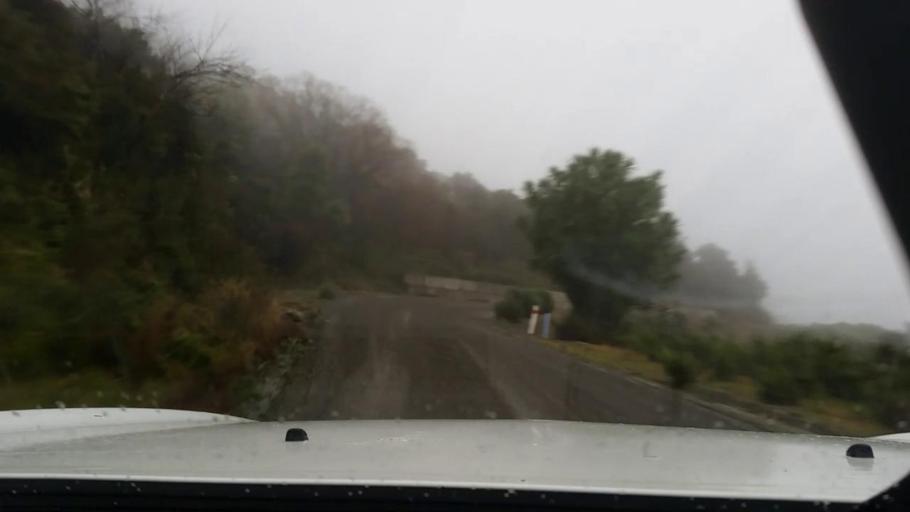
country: NZ
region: Wellington
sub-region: Masterton District
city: Masterton
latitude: -41.2451
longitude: 175.8779
